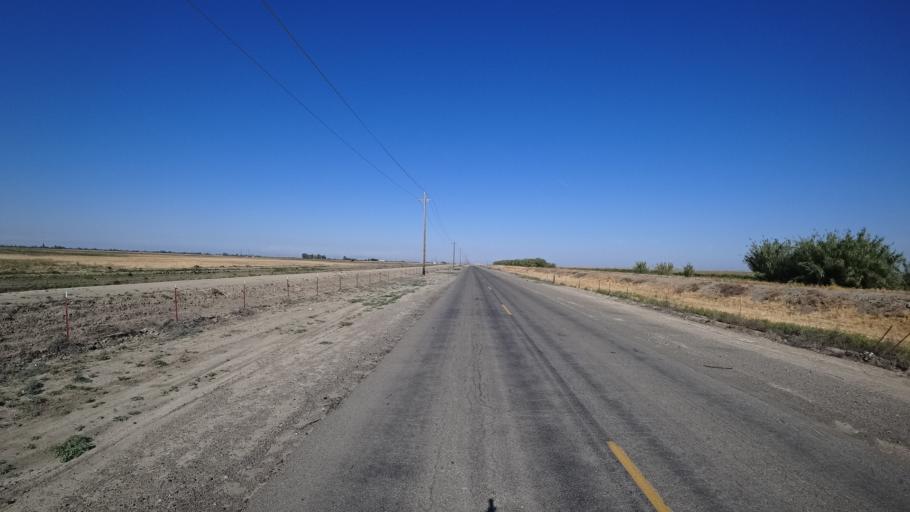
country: US
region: California
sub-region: Kings County
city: Corcoran
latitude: 36.1379
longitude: -119.5423
